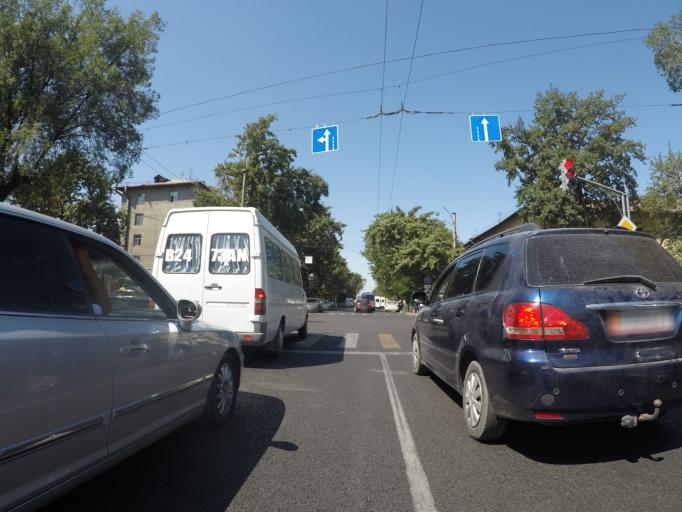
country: KG
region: Chuy
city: Bishkek
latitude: 42.8772
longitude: 74.5755
